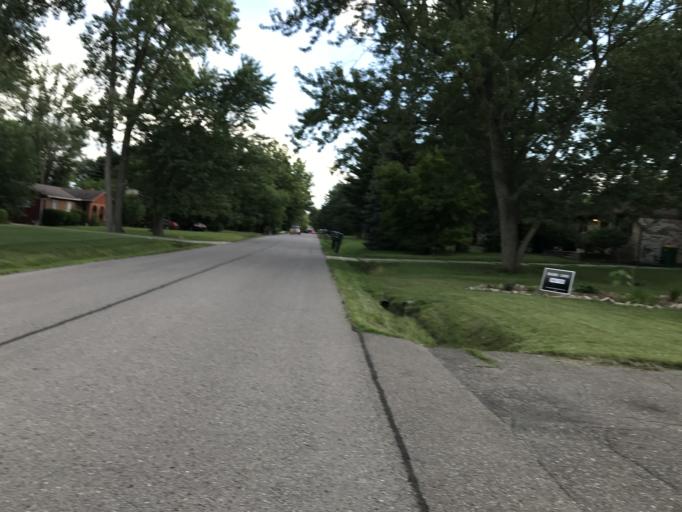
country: US
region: Michigan
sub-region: Oakland County
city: Farmington
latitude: 42.4675
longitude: -83.3497
